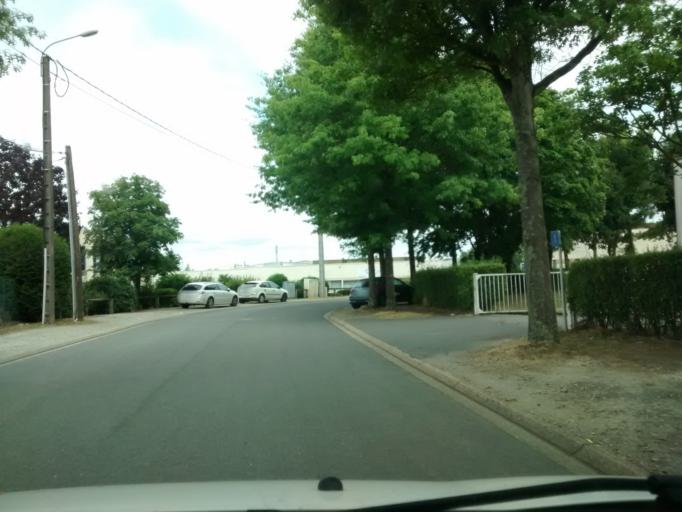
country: FR
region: Brittany
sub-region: Departement d'Ille-et-Vilaine
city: Chantepie
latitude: 48.1038
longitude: -1.6284
